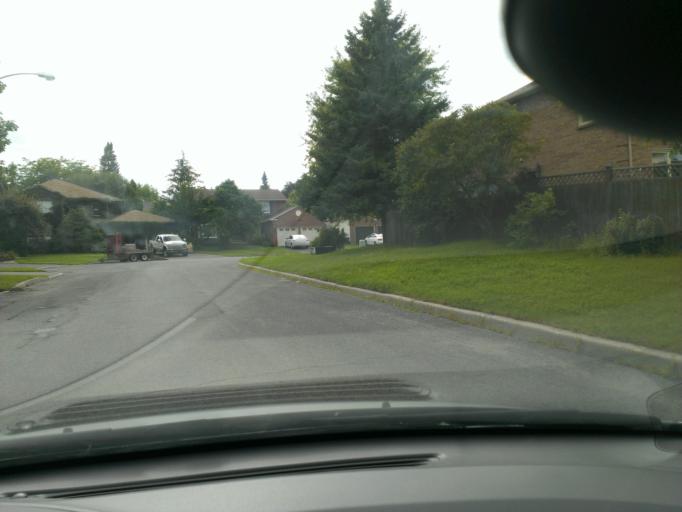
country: CA
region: Quebec
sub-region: Outaouais
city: Gatineau
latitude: 45.4843
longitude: -75.4936
